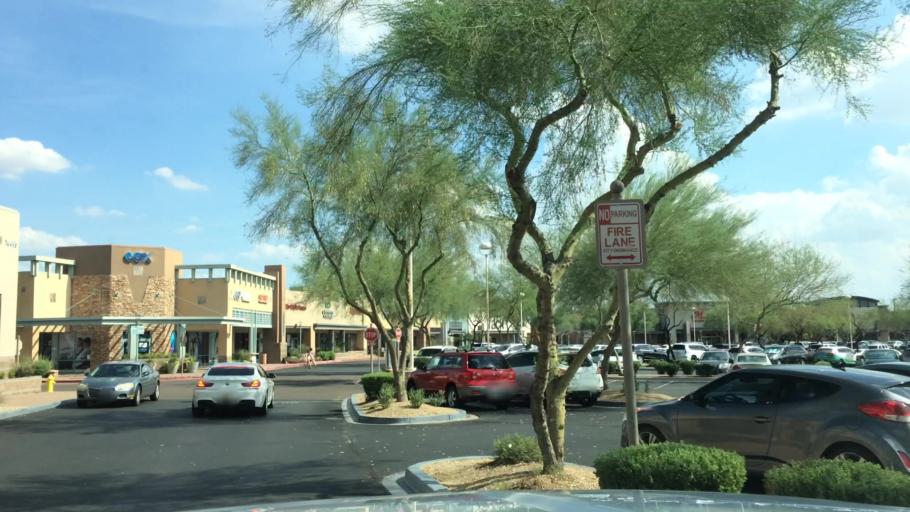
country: US
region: Arizona
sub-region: Maricopa County
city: Paradise Valley
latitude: 33.6357
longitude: -111.9215
